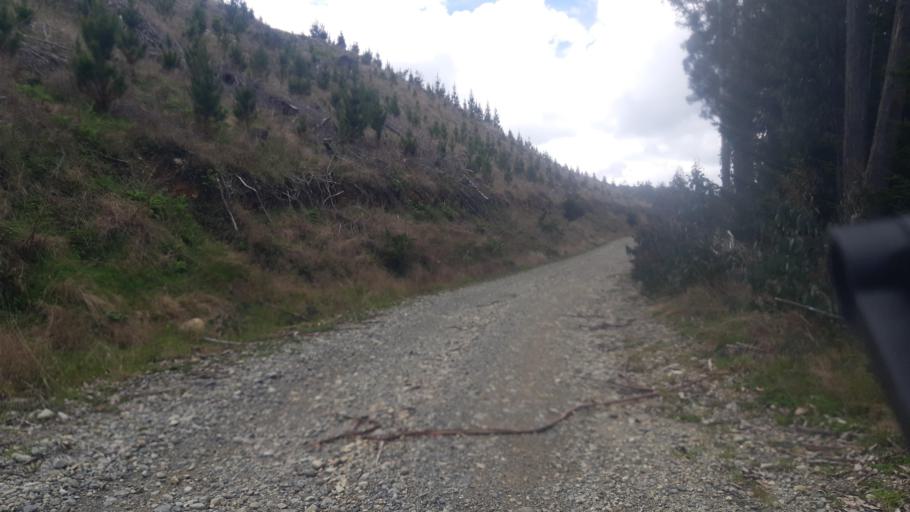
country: NZ
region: Tasman
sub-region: Tasman District
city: Wakefield
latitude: -41.7691
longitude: 172.7980
